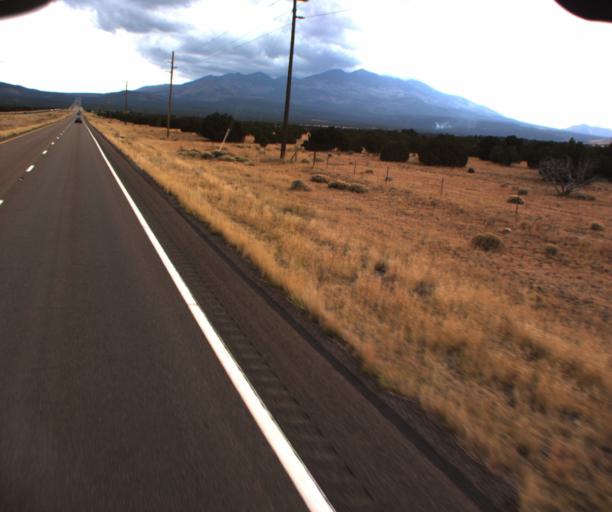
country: US
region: Arizona
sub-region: Coconino County
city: Flagstaff
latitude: 35.4641
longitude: -111.5598
